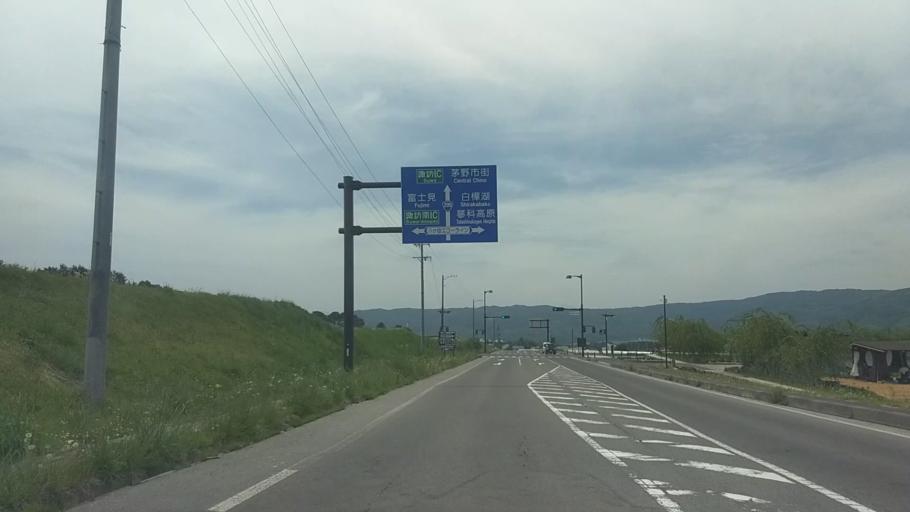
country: JP
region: Nagano
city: Chino
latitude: 36.0253
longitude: 138.2263
